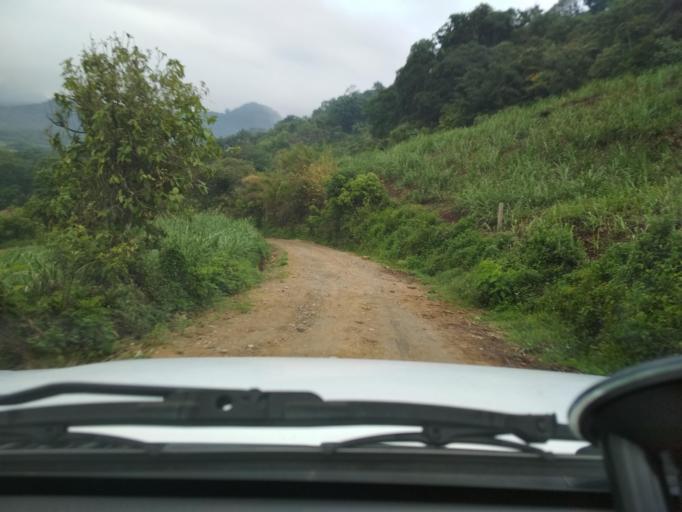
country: MX
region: Veracruz
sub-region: Fortin
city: Monte Salas
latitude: 18.9233
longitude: -97.0393
